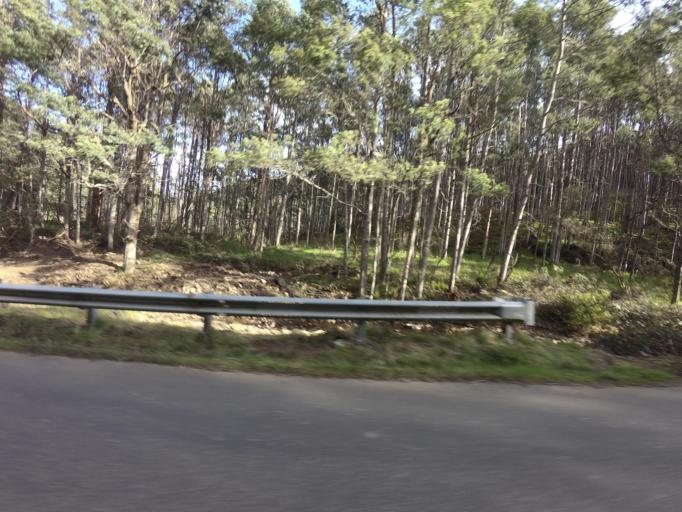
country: AU
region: Tasmania
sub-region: Huon Valley
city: Huonville
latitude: -43.0350
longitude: 147.1440
